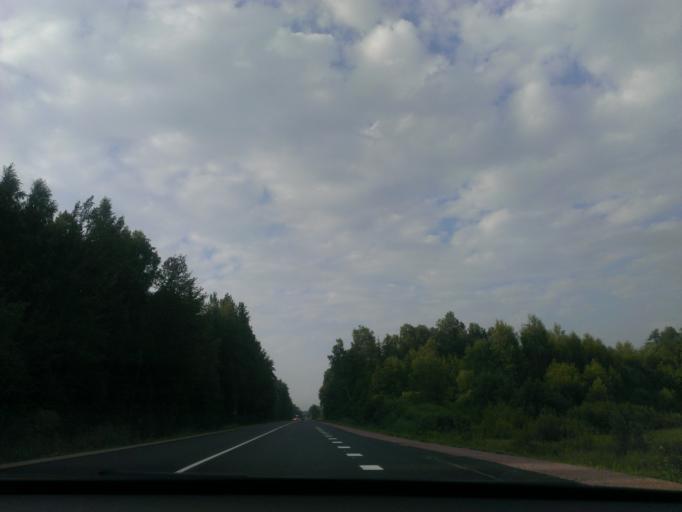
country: LV
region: Lecava
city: Iecava
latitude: 56.6946
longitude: 24.2421
